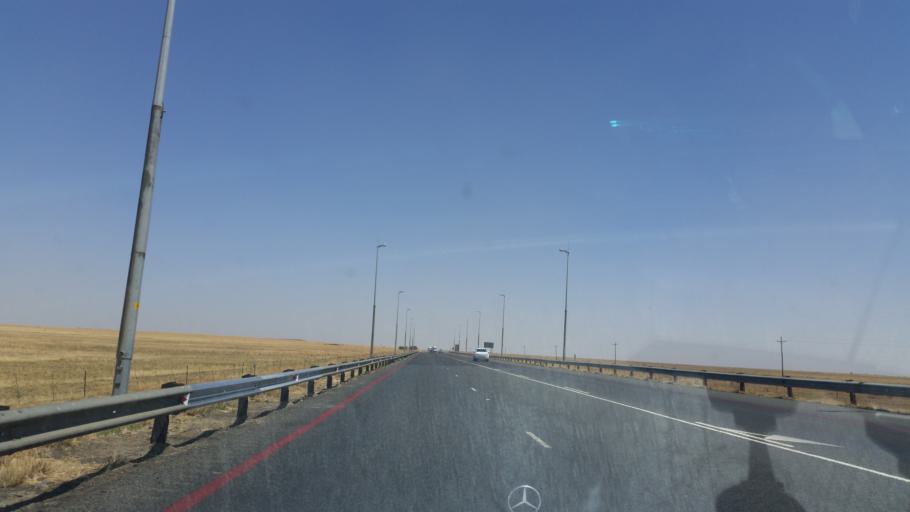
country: ZA
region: Orange Free State
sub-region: Lejweleputswa District Municipality
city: Brandfort
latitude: -28.8003
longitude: 26.6886
